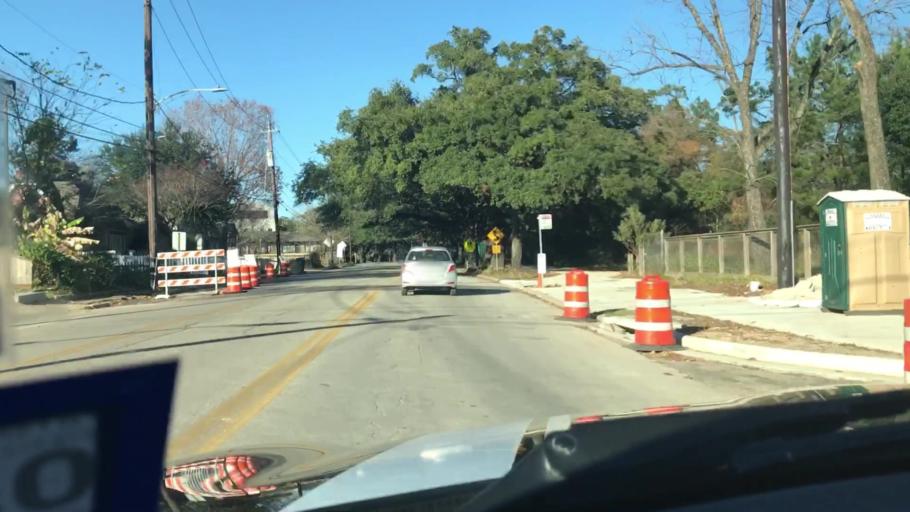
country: US
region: Texas
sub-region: Harris County
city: Houston
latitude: 29.7811
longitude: -95.3723
